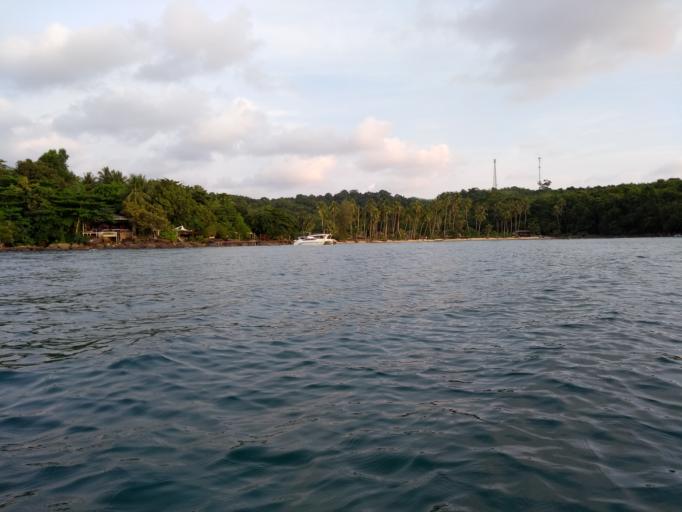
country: TH
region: Trat
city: Ko Kut
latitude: 11.6214
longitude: 102.5414
